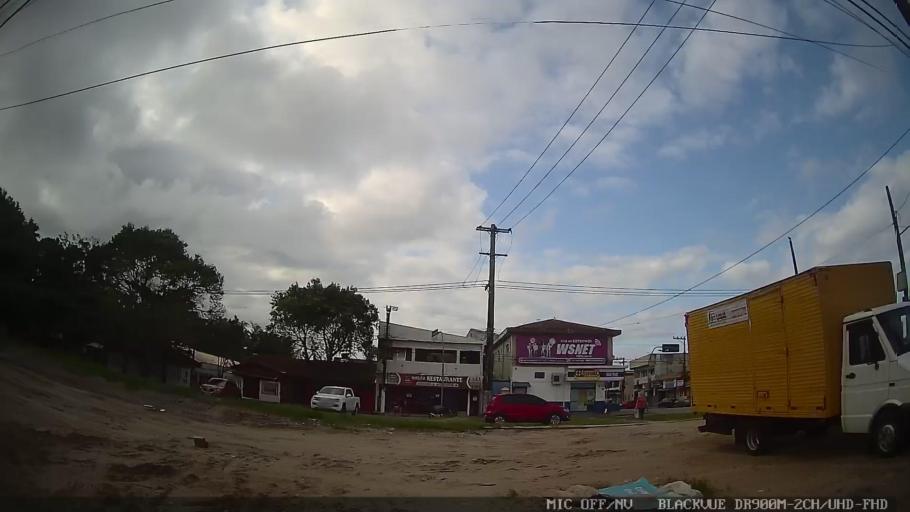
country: BR
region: Sao Paulo
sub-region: Itanhaem
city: Itanhaem
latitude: -24.1934
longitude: -46.8102
